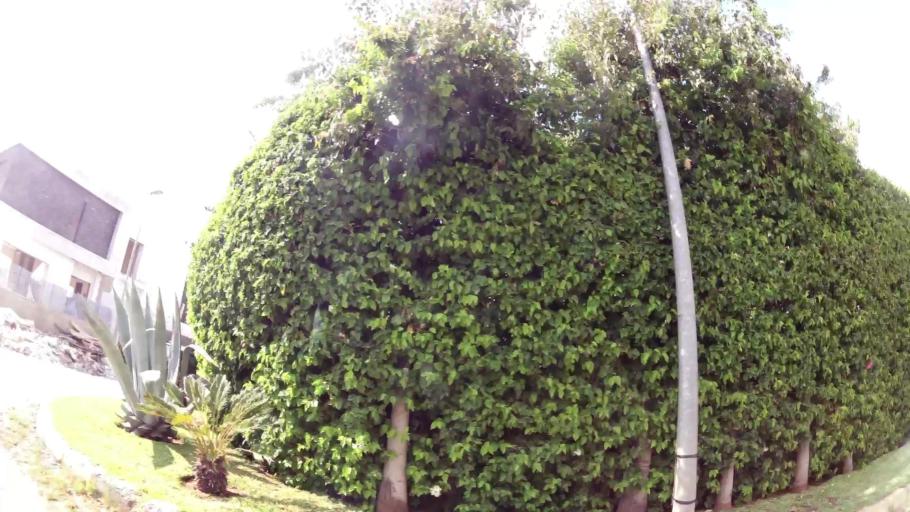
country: MA
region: Rabat-Sale-Zemmour-Zaer
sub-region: Skhirate-Temara
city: Temara
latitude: 33.9482
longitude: -6.8759
